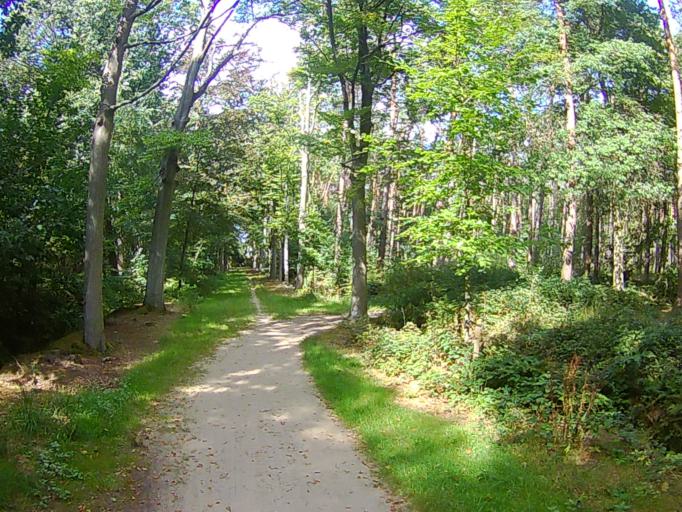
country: BE
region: Flanders
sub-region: Provincie Antwerpen
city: Kapellen
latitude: 51.3332
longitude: 4.4355
